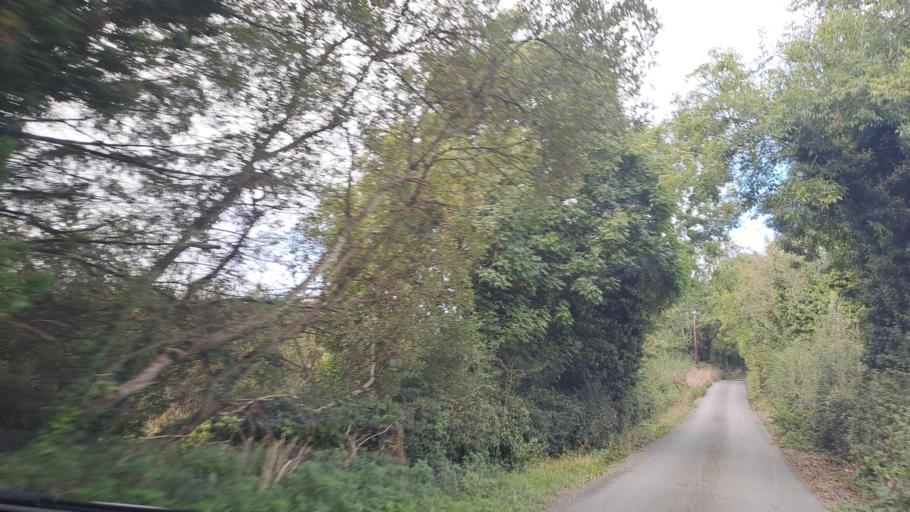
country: IE
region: Ulster
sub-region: An Cabhan
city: Kingscourt
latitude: 53.9904
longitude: -6.8020
